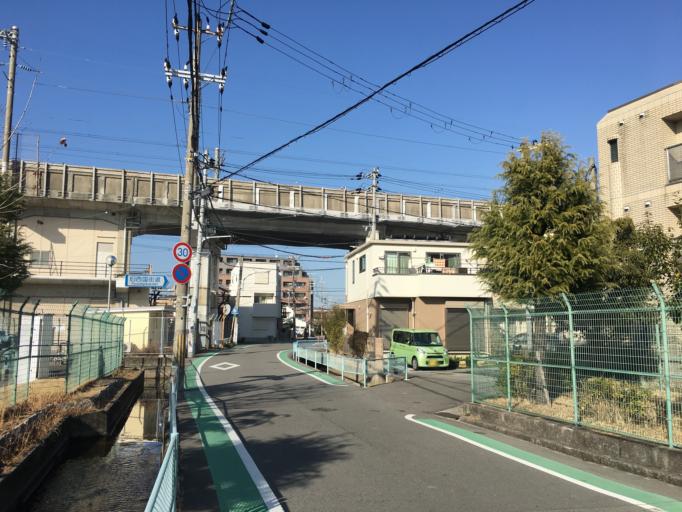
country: JP
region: Hyogo
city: Takarazuka
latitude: 34.7648
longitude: 135.3656
